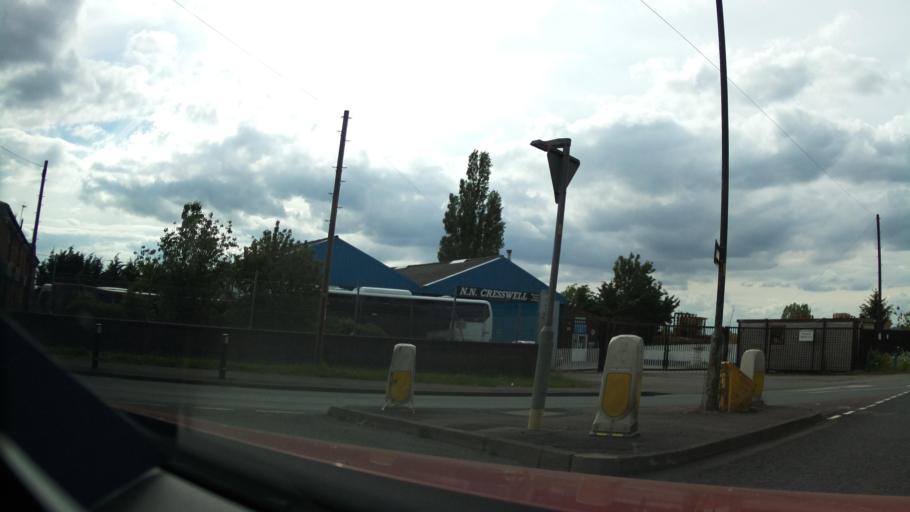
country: GB
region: England
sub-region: Worcestershire
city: Evesham
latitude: 52.1001
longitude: -1.9494
